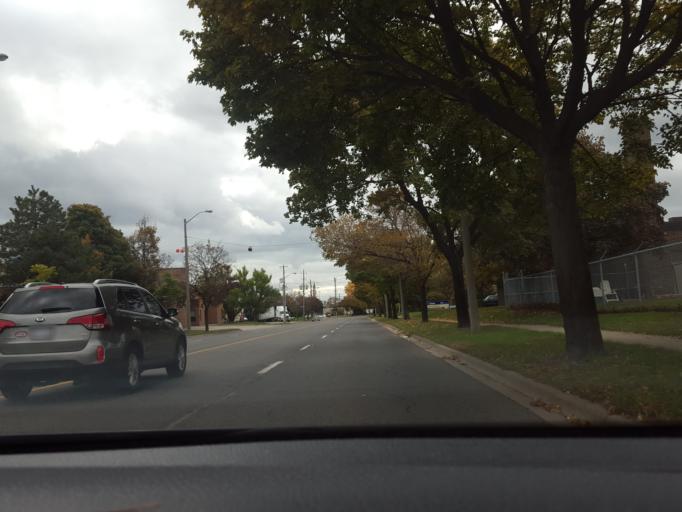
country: CA
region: Ontario
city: Etobicoke
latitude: 43.6242
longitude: -79.5498
